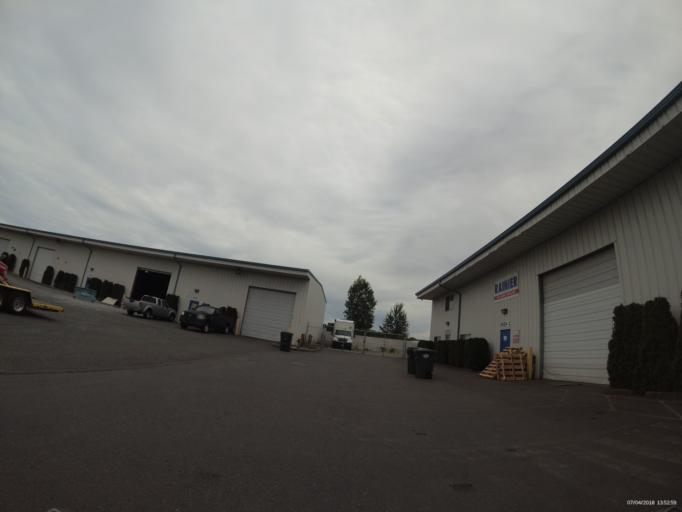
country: US
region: Washington
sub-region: Pierce County
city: McChord Air Force Base
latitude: 47.1545
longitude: -122.4723
